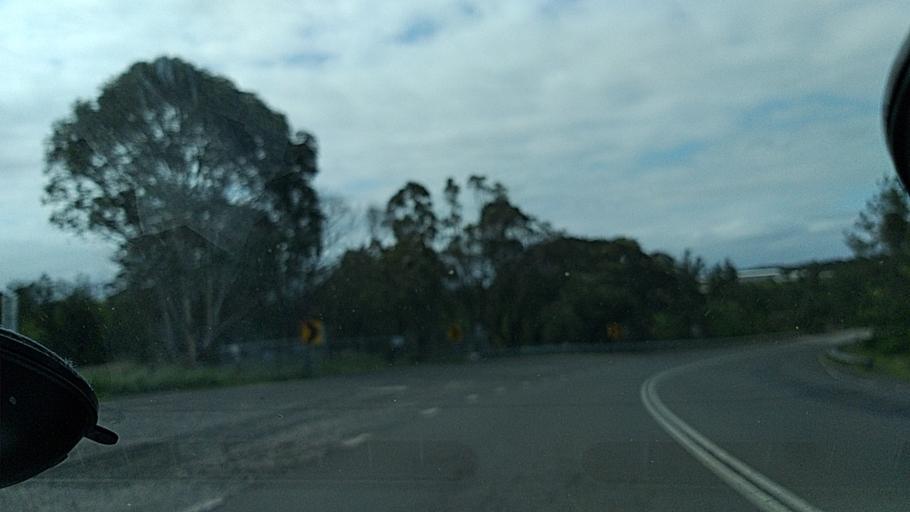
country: AU
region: New South Wales
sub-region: Camden
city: Camden South
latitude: -34.1183
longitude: 150.7388
